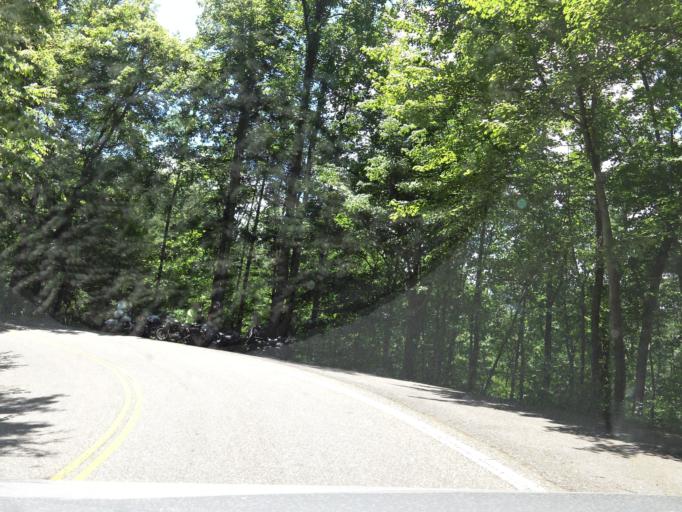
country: US
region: North Carolina
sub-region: Graham County
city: Robbinsville
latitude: 35.4919
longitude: -83.9297
